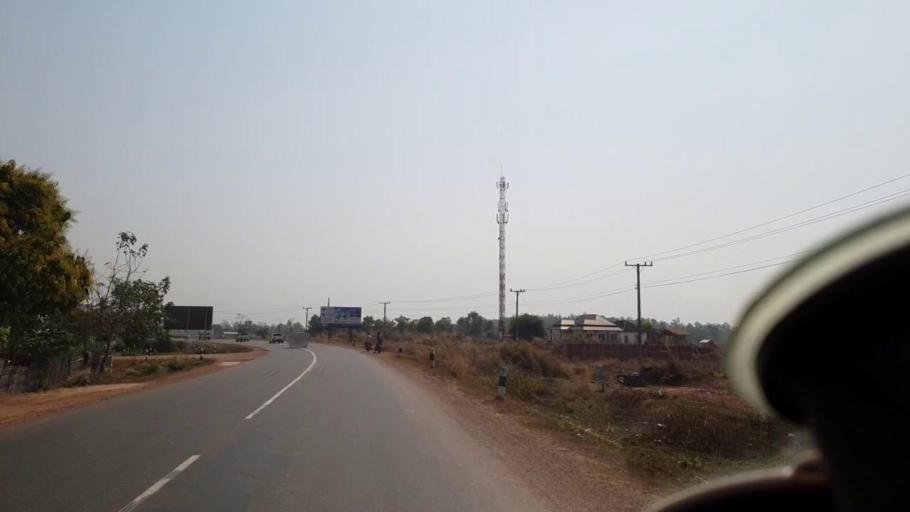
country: TH
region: Nong Khai
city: Phon Phisai
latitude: 18.0468
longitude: 102.8799
